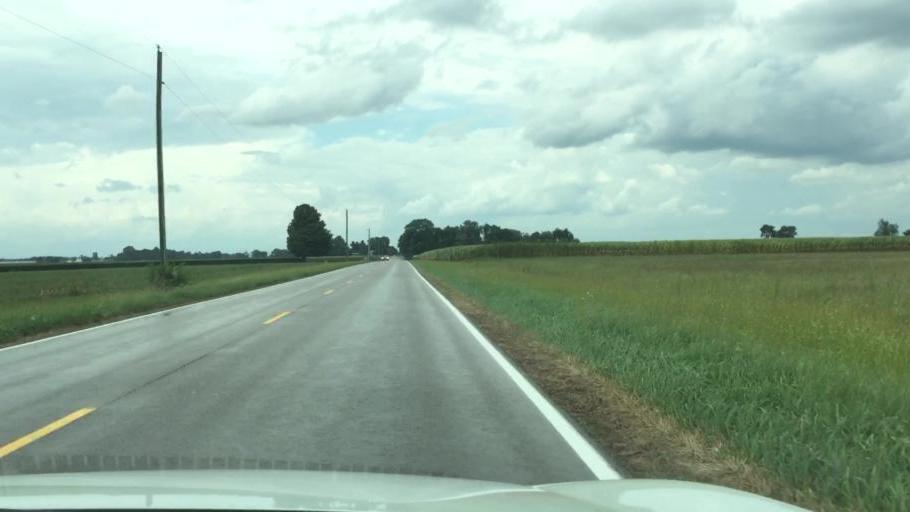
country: US
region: Ohio
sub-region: Champaign County
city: Urbana
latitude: 40.0420
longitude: -83.7099
